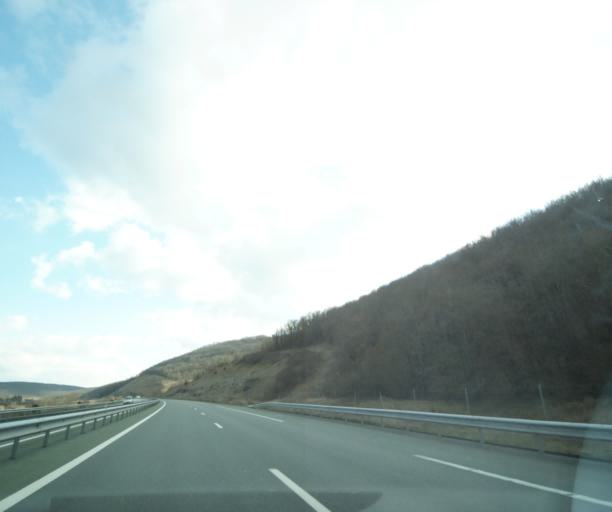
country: FR
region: Midi-Pyrenees
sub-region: Departement du Lot
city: Le Vigan
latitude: 44.8002
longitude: 1.5090
